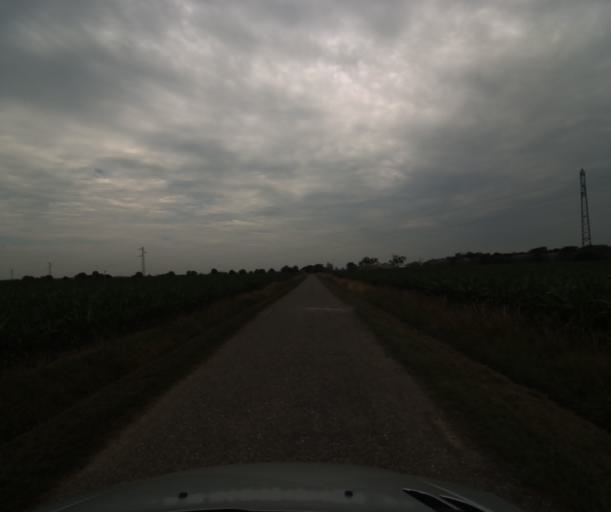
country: FR
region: Midi-Pyrenees
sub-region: Departement de la Haute-Garonne
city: Lacasse
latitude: 43.4263
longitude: 1.2758
